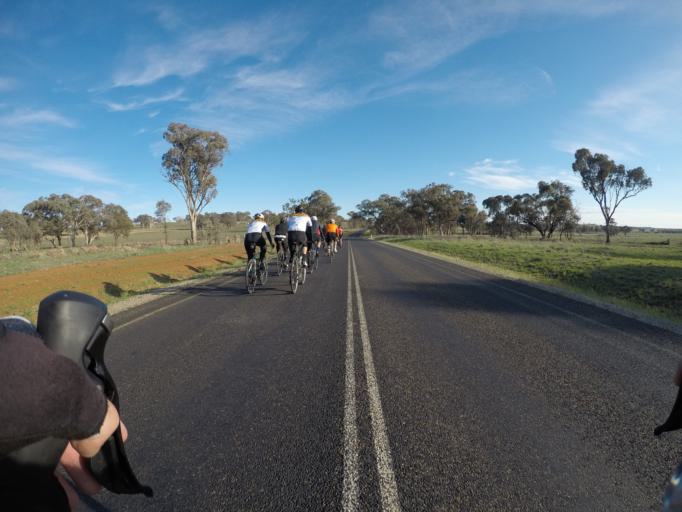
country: AU
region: New South Wales
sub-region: Cabonne
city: Molong
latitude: -32.9747
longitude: 148.7848
